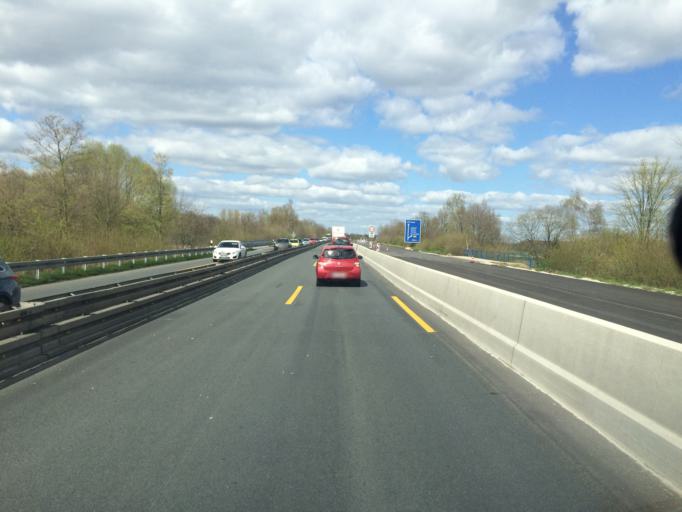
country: DE
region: North Rhine-Westphalia
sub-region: Regierungsbezirk Munster
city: Legden
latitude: 52.0462
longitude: 7.0616
